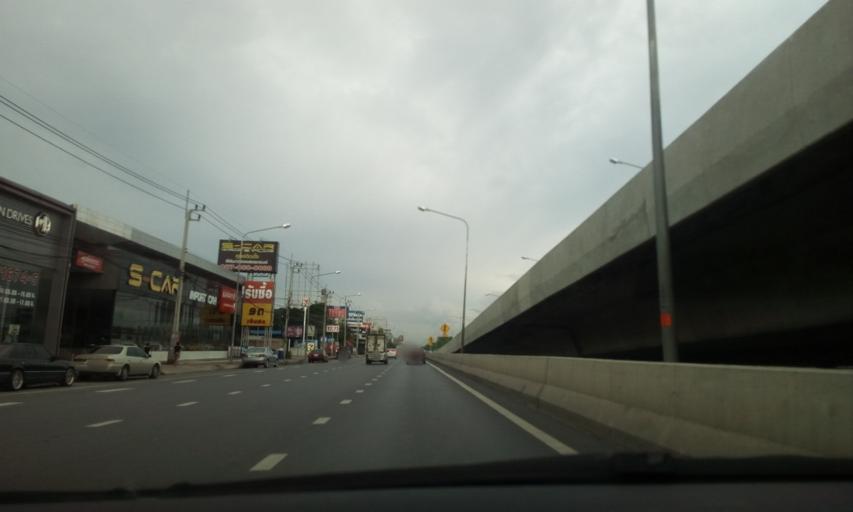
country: TH
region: Nonthaburi
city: Bang Bua Thong
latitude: 13.9269
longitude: 100.4586
